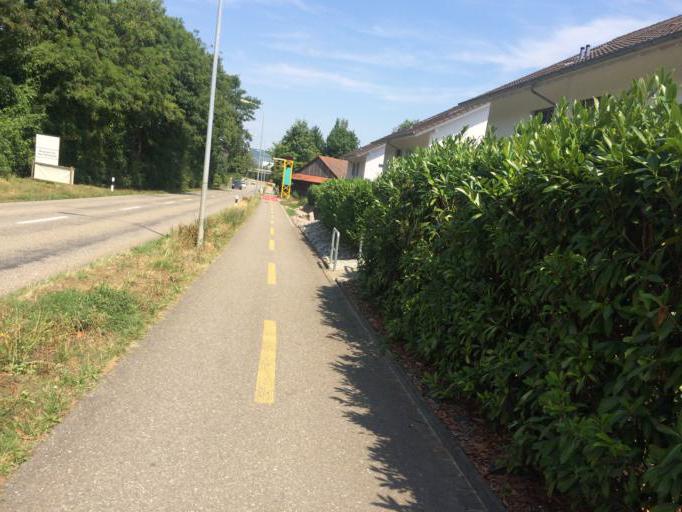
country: CH
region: Aargau
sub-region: Bezirk Brugg
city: Villigen
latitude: 47.5297
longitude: 8.2159
